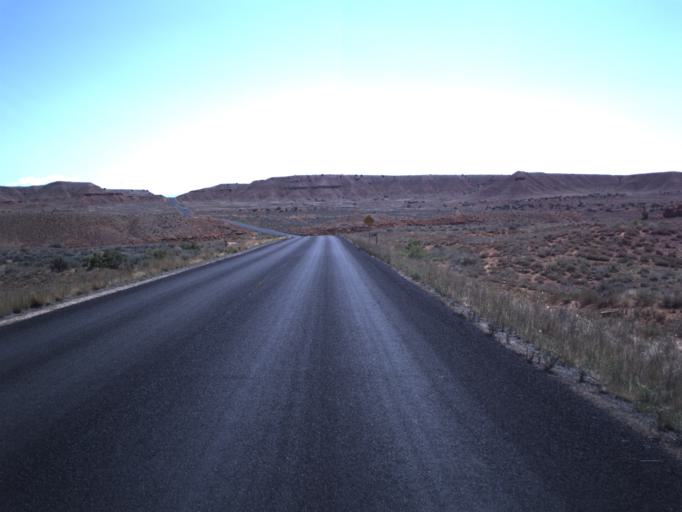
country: US
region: Utah
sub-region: Uintah County
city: Maeser
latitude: 40.4127
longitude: -109.7371
